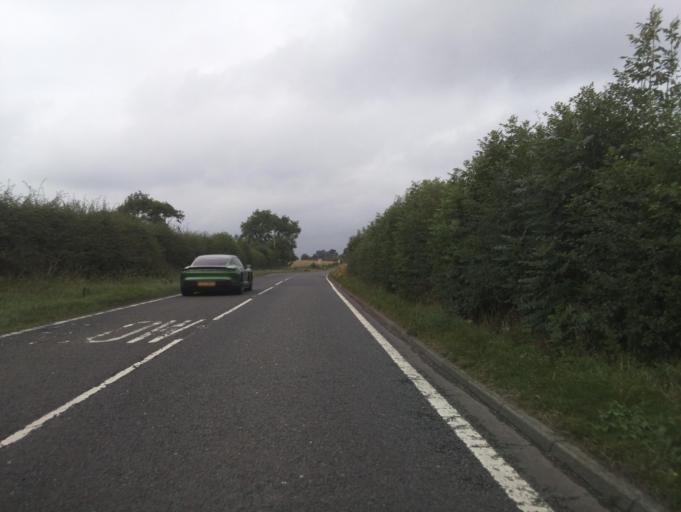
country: GB
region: England
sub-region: Northumberland
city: Hartburn
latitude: 55.1134
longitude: -1.8846
